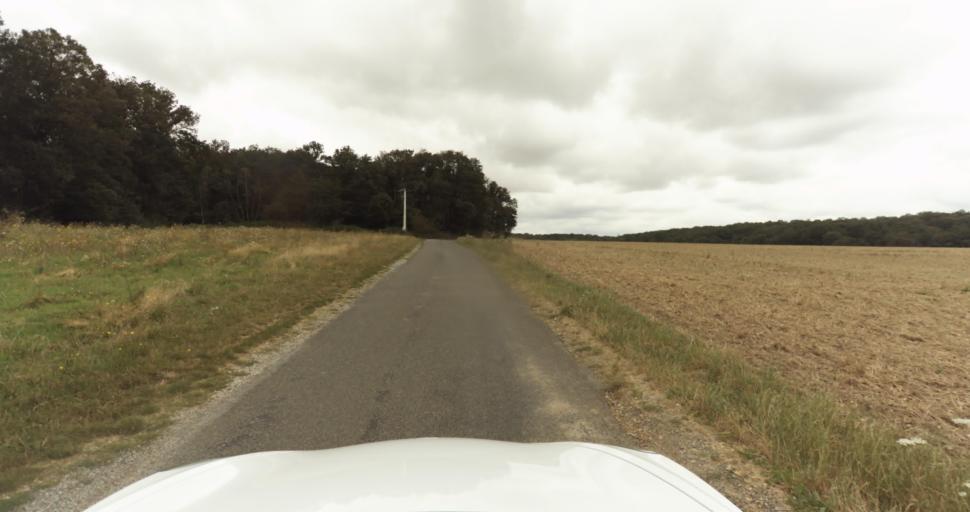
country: FR
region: Haute-Normandie
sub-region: Departement de l'Eure
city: Saint-Sebastien-de-Morsent
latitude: 49.0230
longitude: 1.0609
